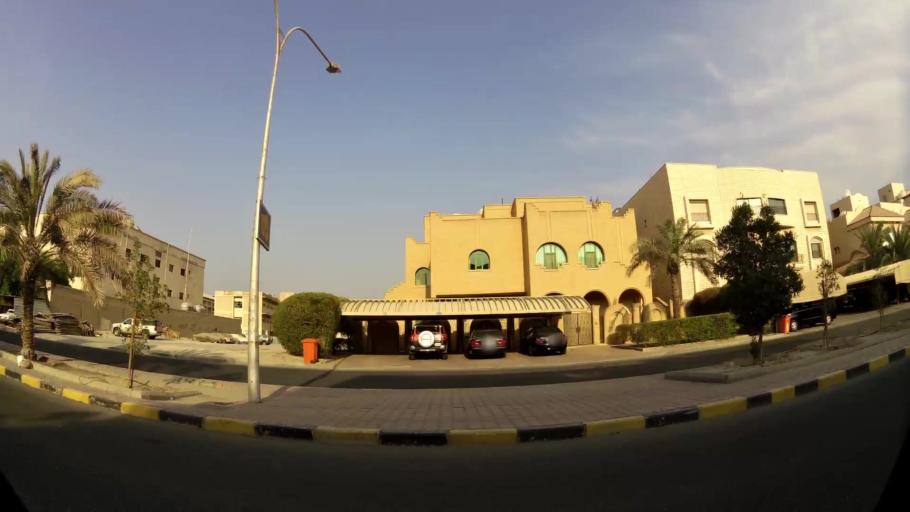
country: KW
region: Muhafazat Hawalli
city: Hawalli
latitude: 29.3101
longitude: 48.0144
